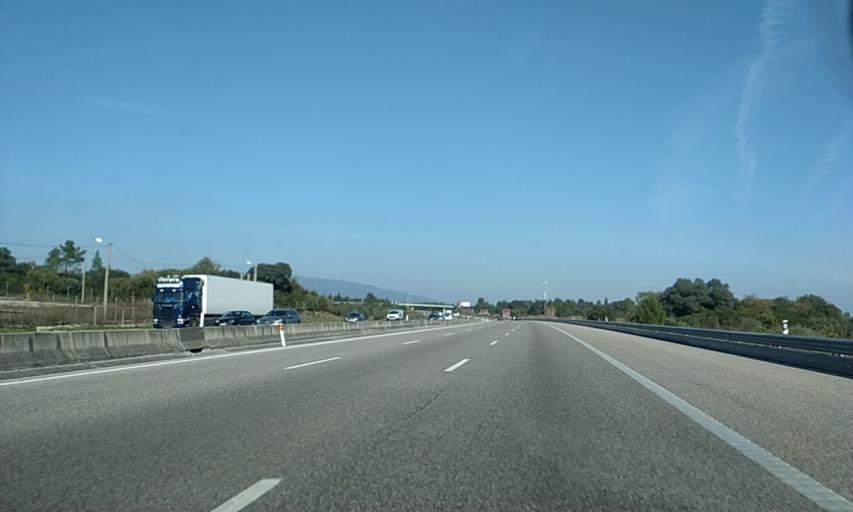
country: PT
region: Santarem
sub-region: Alcanena
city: Alcanena
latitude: 39.4282
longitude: -8.6293
